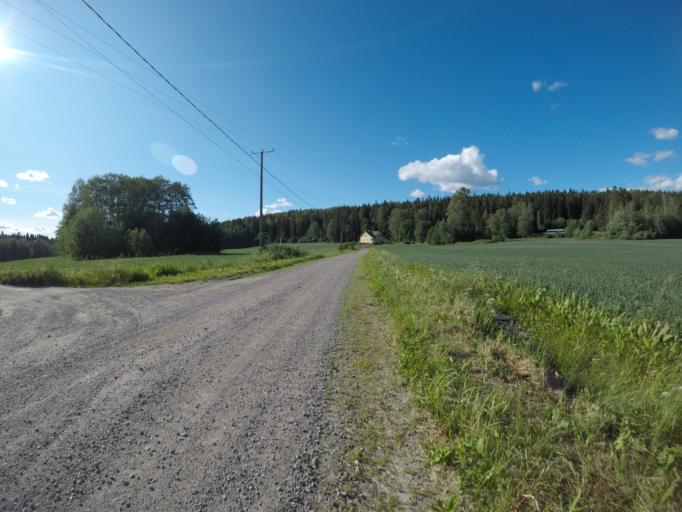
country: FI
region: Haeme
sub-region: Haemeenlinna
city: Haemeenlinna
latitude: 61.0211
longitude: 24.4997
